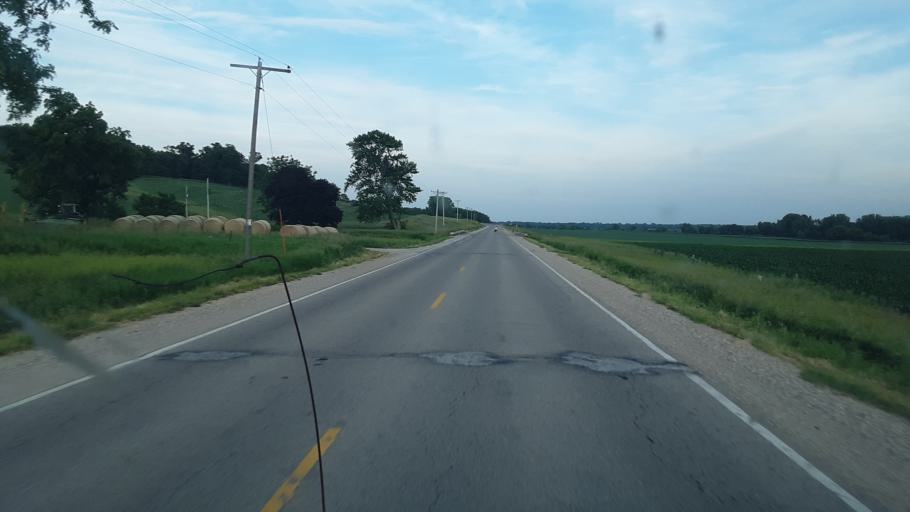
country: US
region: Iowa
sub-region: Benton County
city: Belle Plaine
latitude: 41.9089
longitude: -92.3396
